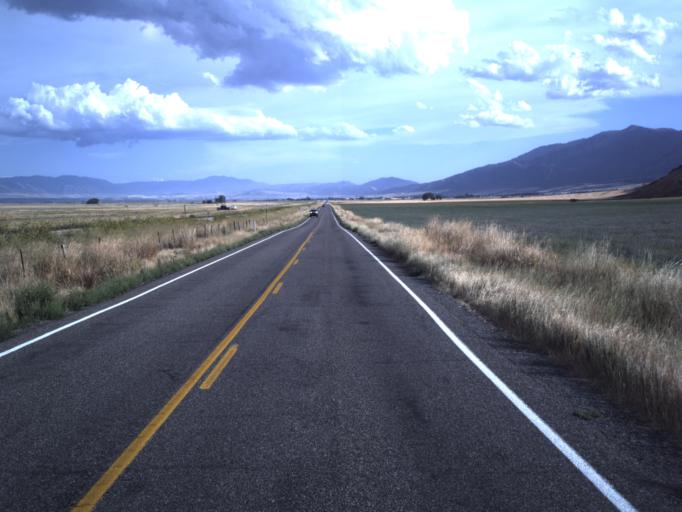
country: US
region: Utah
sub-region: Cache County
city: Benson
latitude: 41.8093
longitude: -111.9947
